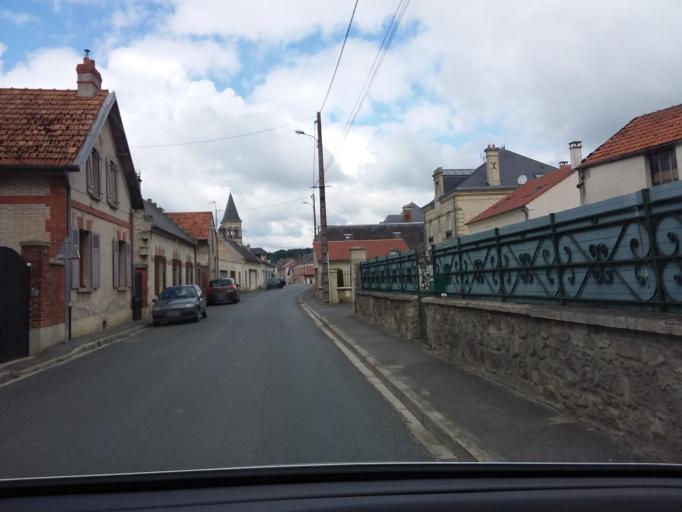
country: FR
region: Picardie
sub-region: Departement de l'Aisne
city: Vailly-sur-Aisne
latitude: 49.4093
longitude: 3.5210
